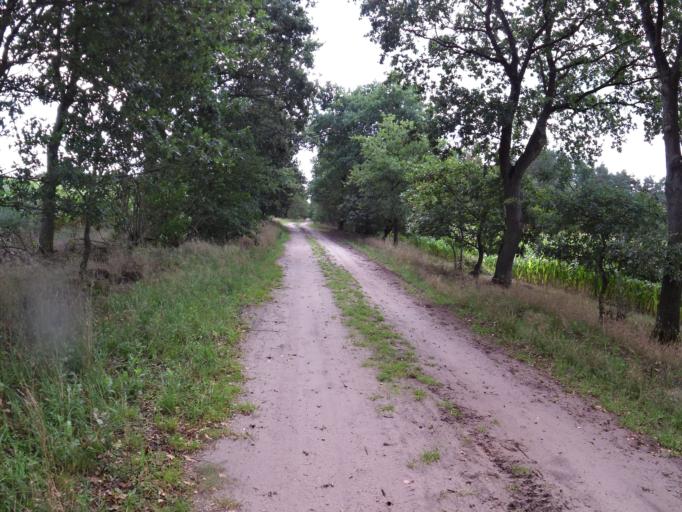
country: DE
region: Lower Saxony
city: Sandbostel
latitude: 53.3746
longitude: 9.1501
